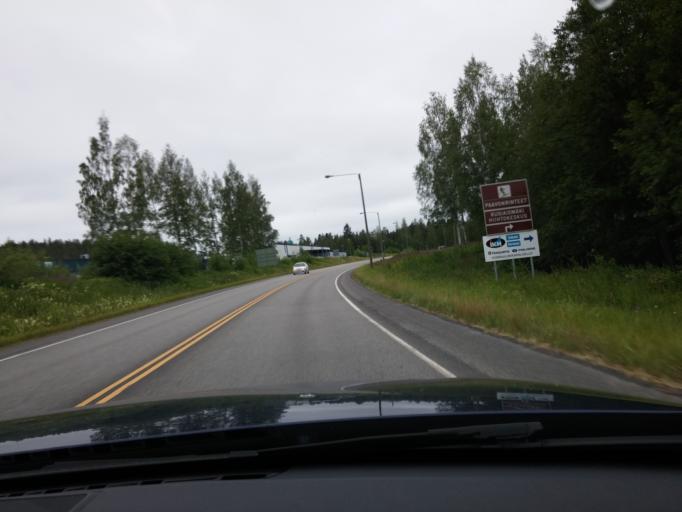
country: FI
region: Central Finland
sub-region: Saarijaervi-Viitasaari
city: Saarijaervi
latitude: 62.6877
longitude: 25.3111
